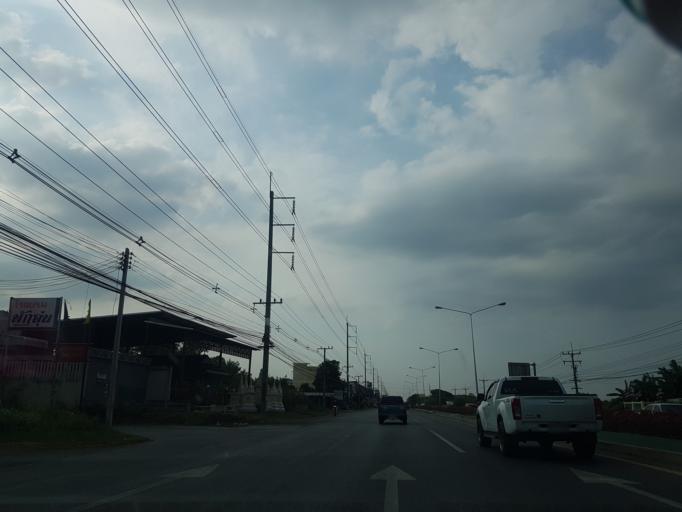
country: TH
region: Sara Buri
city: Phra Phutthabat
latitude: 14.7367
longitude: 100.7735
